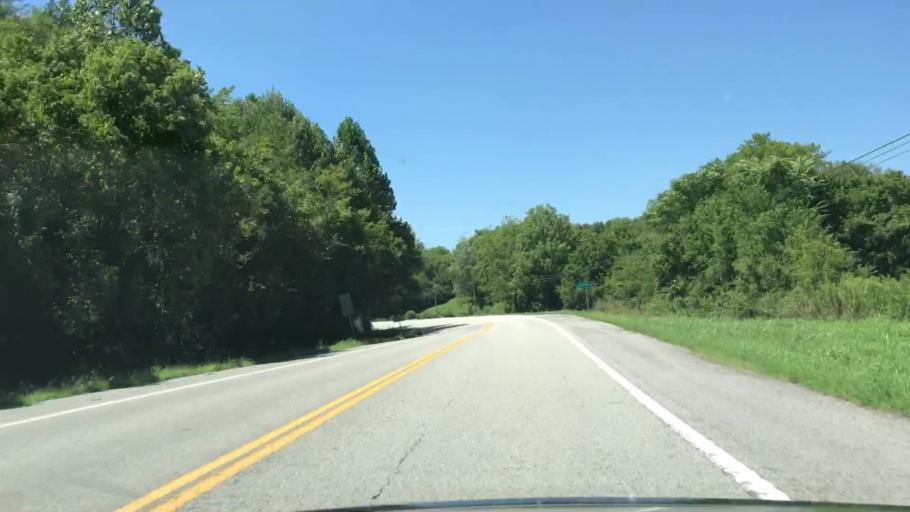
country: US
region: Tennessee
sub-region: Clay County
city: Celina
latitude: 36.4730
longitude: -85.5802
